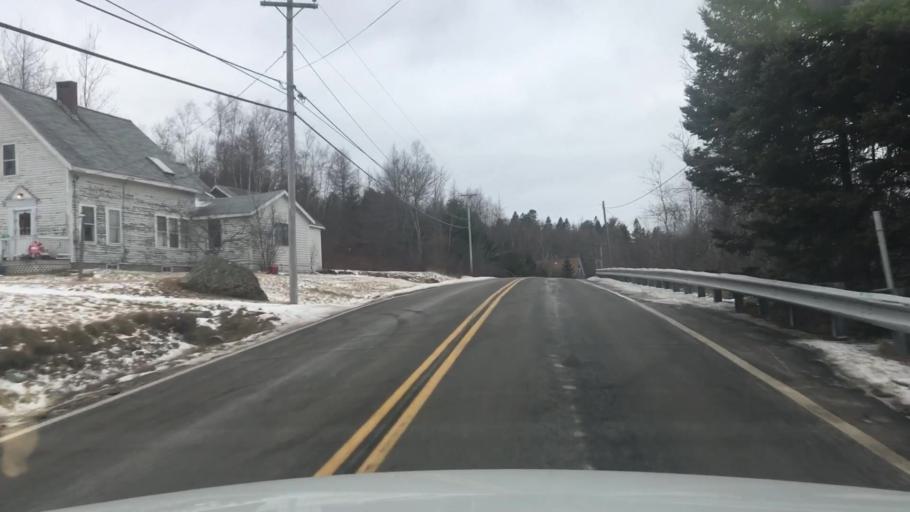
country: US
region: Maine
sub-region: Washington County
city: East Machias
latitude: 44.7263
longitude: -67.3878
